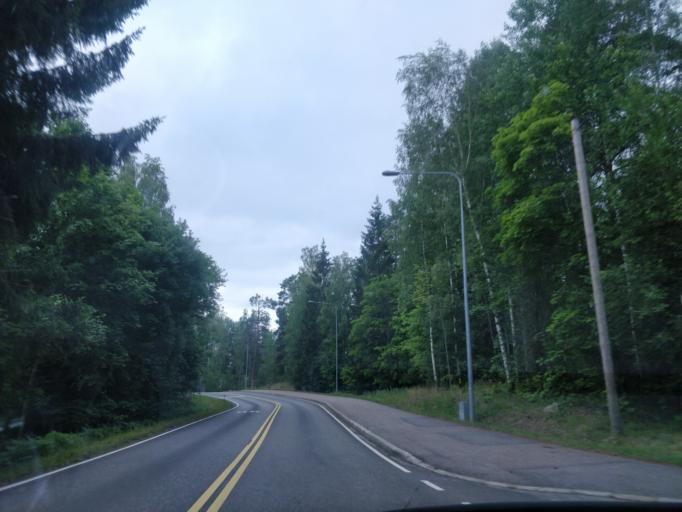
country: FI
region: Uusimaa
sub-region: Helsinki
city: Kauniainen
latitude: 60.2596
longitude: 24.7032
